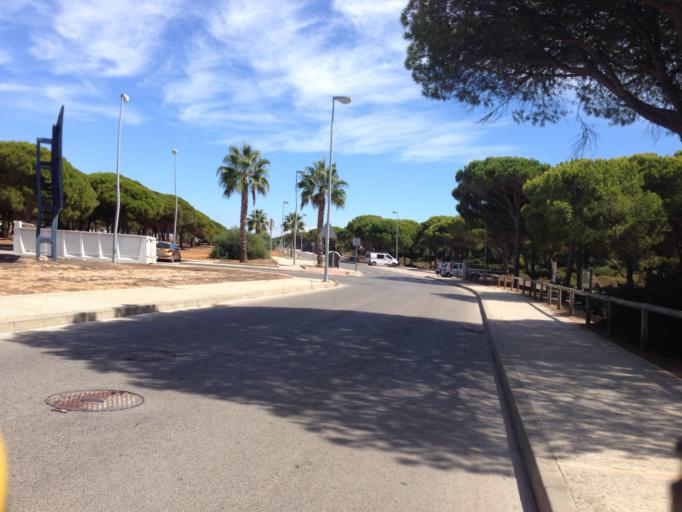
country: ES
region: Andalusia
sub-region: Provincia de Cadiz
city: Chiclana de la Frontera
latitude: 36.3789
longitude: -6.1979
